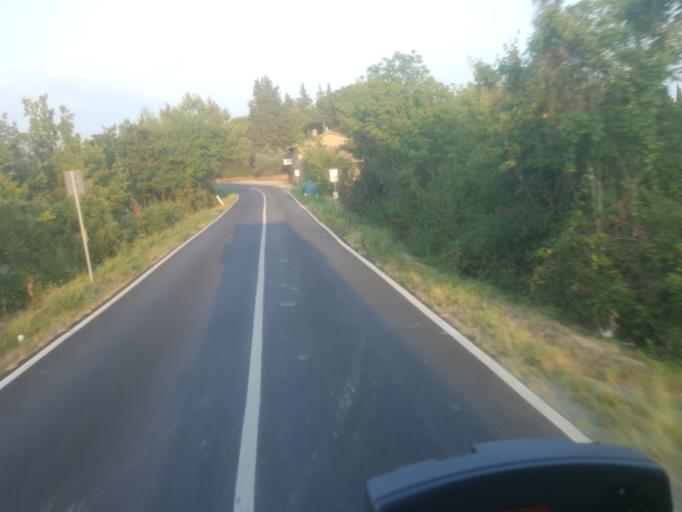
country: IT
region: Tuscany
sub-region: Province of Florence
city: Certaldo
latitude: 43.5443
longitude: 11.0015
